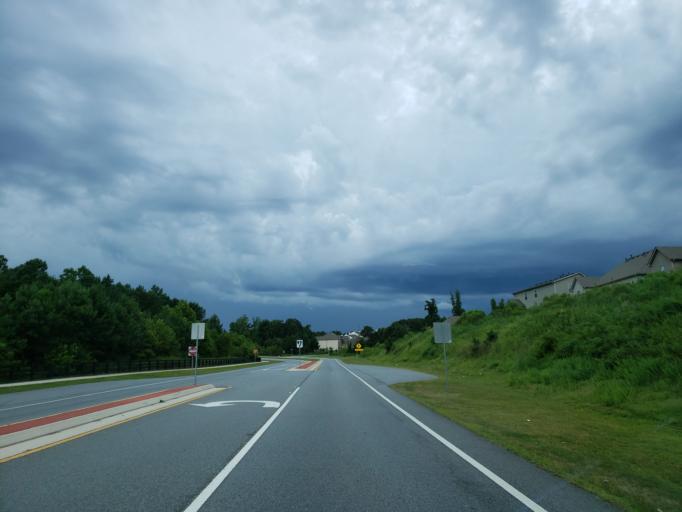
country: US
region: Georgia
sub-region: Bartow County
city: Emerson
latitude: 34.0307
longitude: -84.7706
